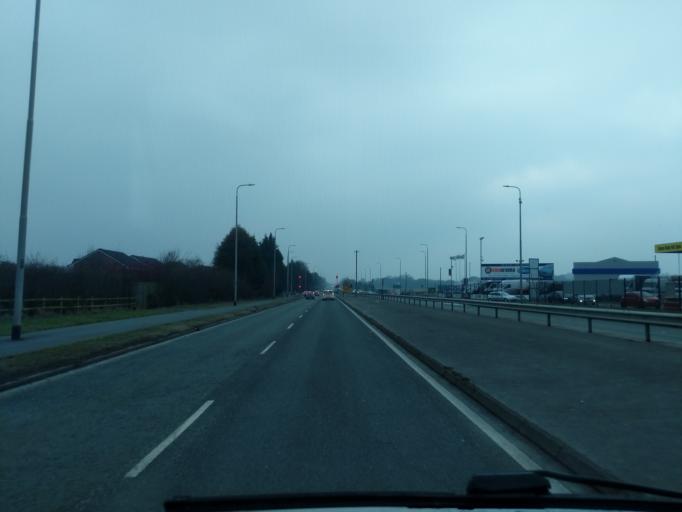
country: GB
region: England
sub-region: St. Helens
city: Haydock
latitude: 53.4725
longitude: -2.6684
